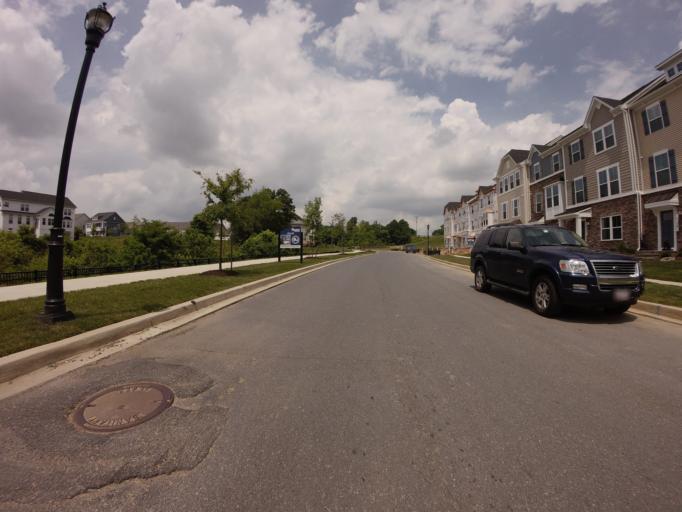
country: US
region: Maryland
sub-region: Frederick County
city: Brunswick
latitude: 39.3290
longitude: -77.6319
